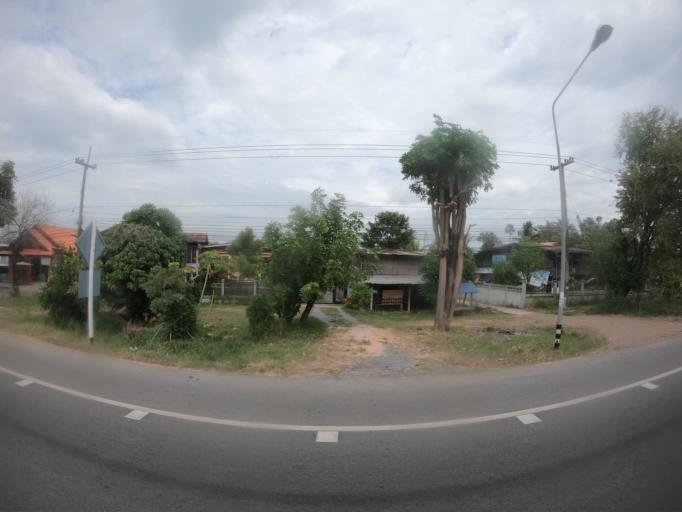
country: TH
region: Maha Sarakham
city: Maha Sarakham
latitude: 16.1552
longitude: 103.3712
